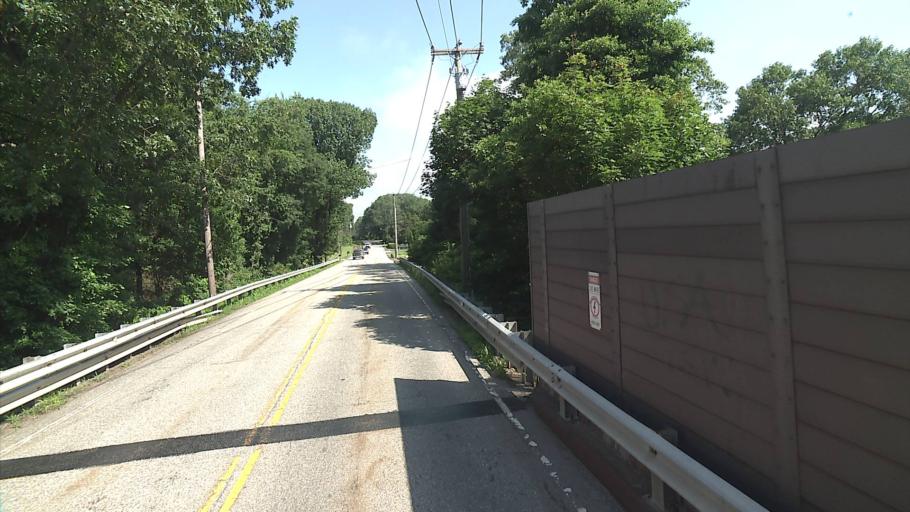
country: US
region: Connecticut
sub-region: Middlesex County
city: Clinton
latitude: 41.2777
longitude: -72.4853
